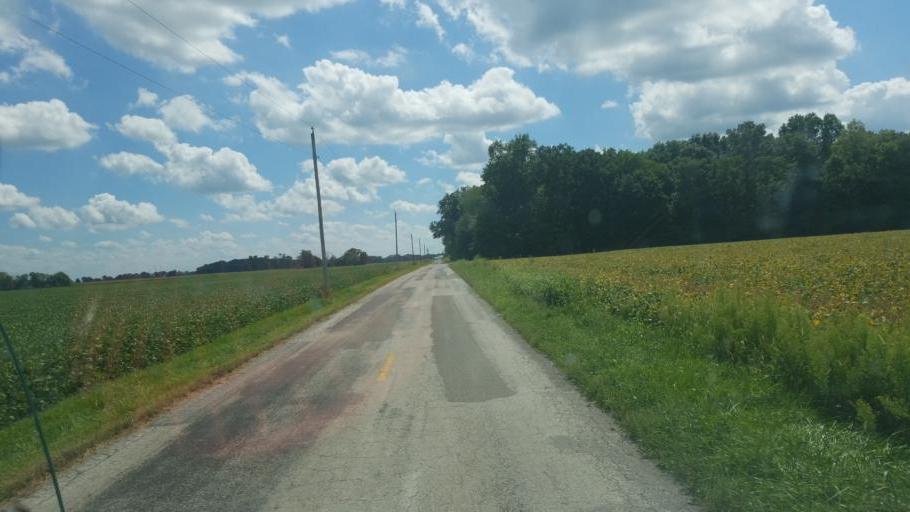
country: US
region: Ohio
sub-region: Marion County
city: Prospect
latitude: 40.4780
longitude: -83.1666
